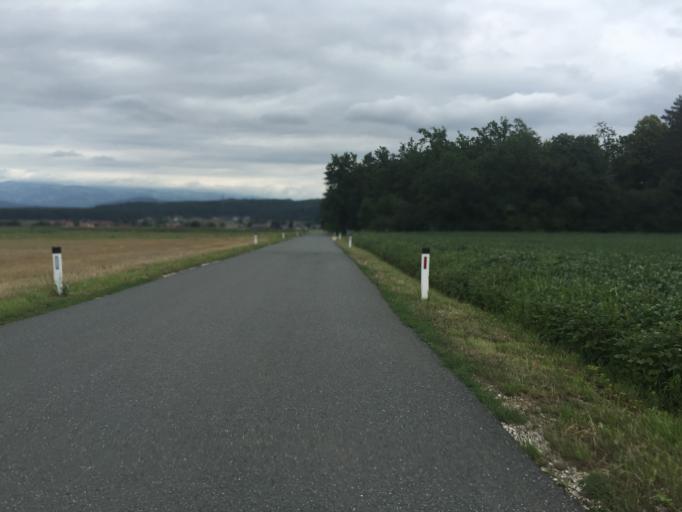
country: AT
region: Carinthia
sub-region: Politischer Bezirk Volkermarkt
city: Feistritz ob Bleiburg
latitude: 46.5610
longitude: 14.7673
